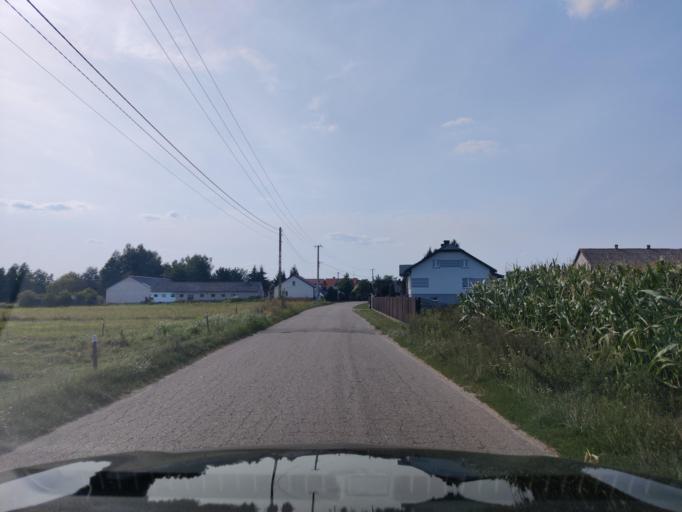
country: PL
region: Masovian Voivodeship
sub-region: Powiat wyszkowski
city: Rzasnik
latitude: 52.7396
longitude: 21.3358
